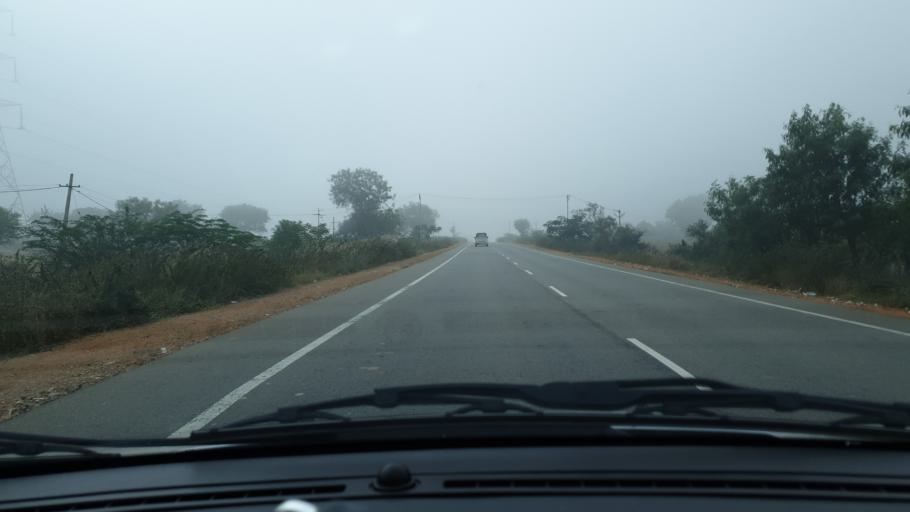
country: IN
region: Telangana
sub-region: Nalgonda
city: Devarkonda
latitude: 16.5985
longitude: 78.6813
